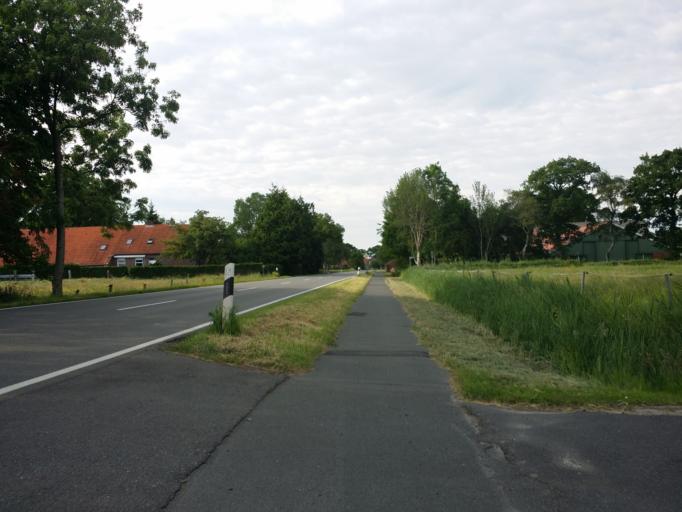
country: DE
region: Lower Saxony
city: Wittmund
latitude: 53.5448
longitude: 7.7821
